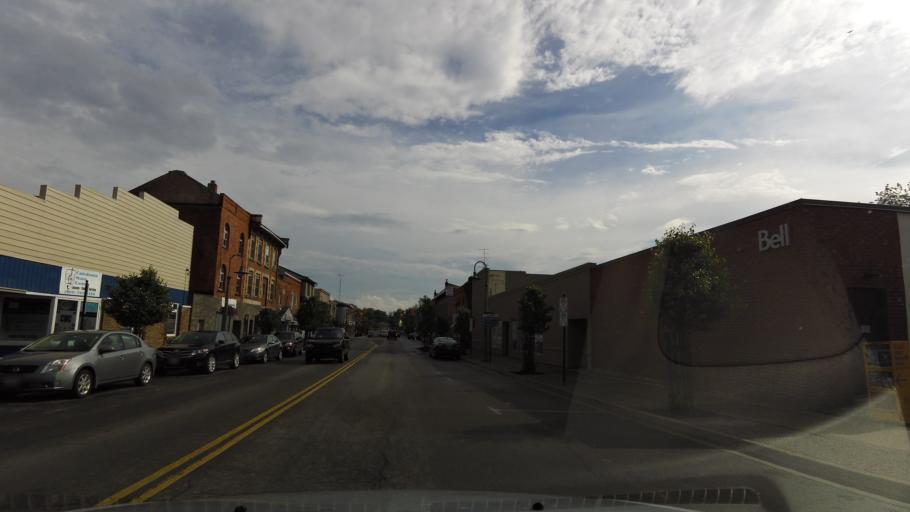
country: CA
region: Ontario
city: Ancaster
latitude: 43.0749
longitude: -79.9514
